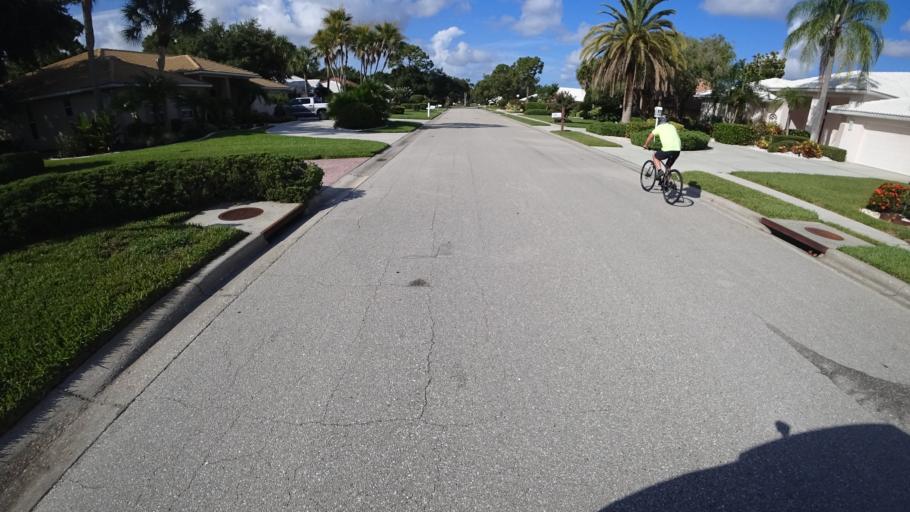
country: US
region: Florida
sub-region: Sarasota County
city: Desoto Lakes
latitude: 27.4065
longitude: -82.4822
